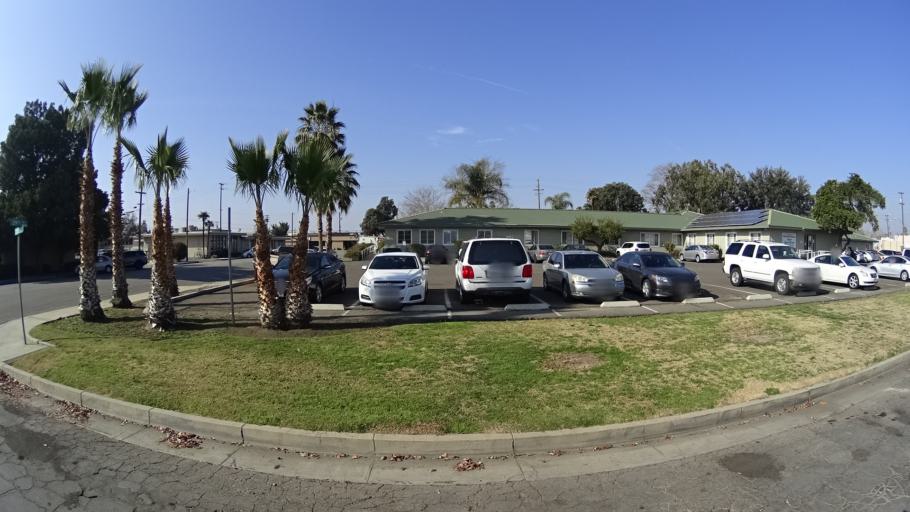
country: US
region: California
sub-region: Kern County
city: Bakersfield
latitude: 35.3859
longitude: -119.0200
